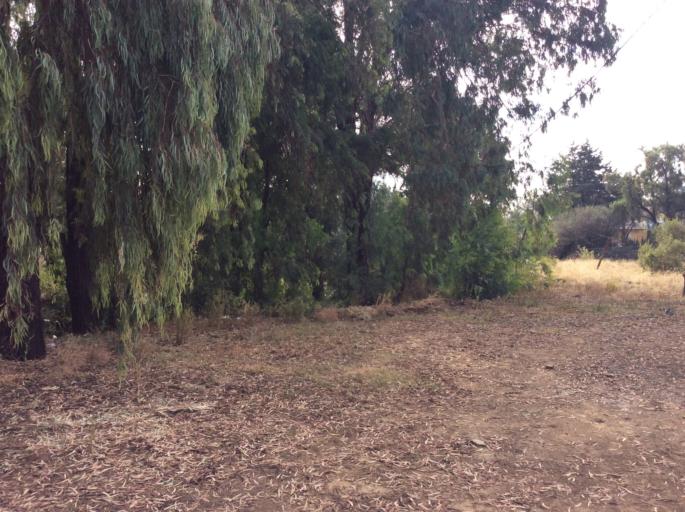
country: ZA
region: Orange Free State
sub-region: Xhariep District Municipality
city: Dewetsdorp
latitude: -29.5898
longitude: 26.6652
